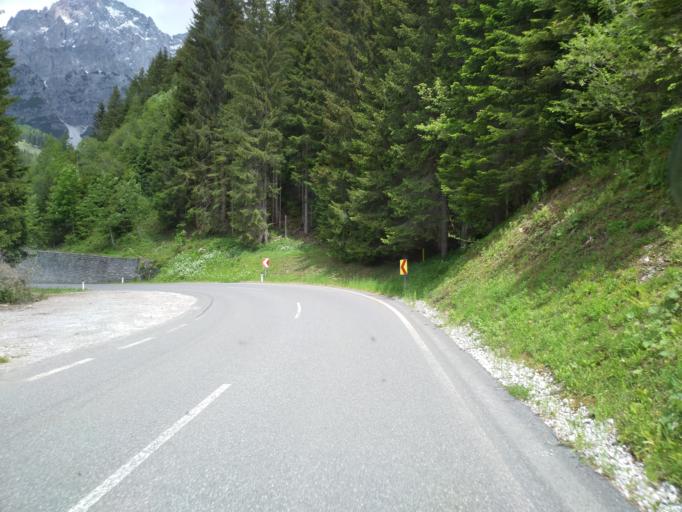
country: AT
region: Salzburg
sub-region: Politischer Bezirk Sankt Johann im Pongau
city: Filzmoos
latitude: 47.4378
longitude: 13.5797
